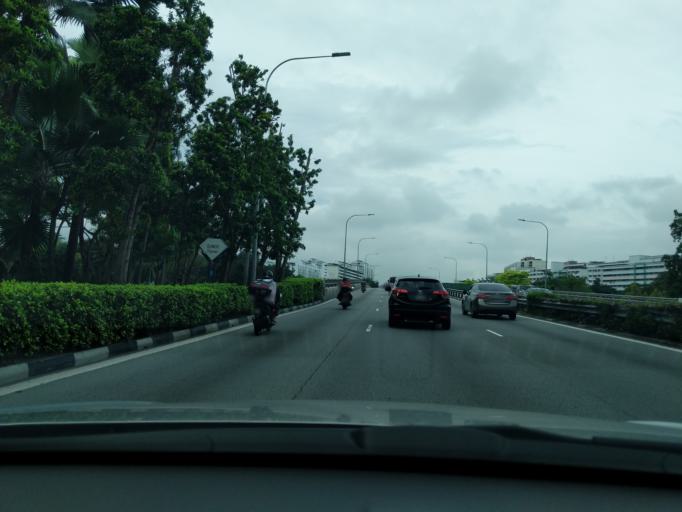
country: SG
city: Singapore
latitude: 1.3266
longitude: 103.9074
